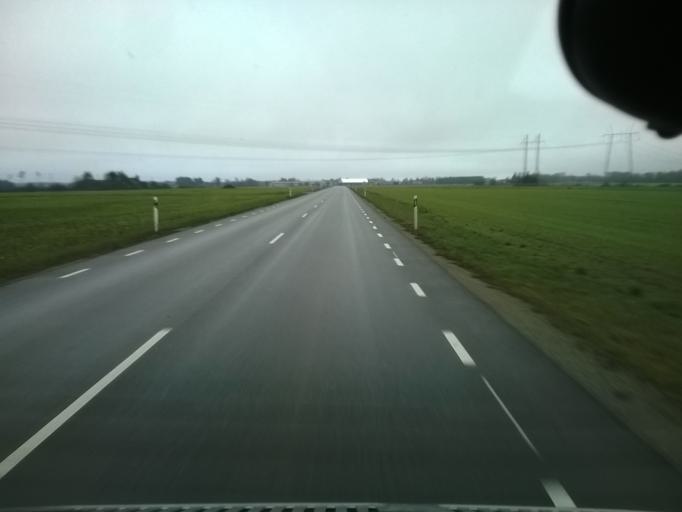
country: EE
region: Harju
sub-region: Saku vald
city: Saku
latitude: 59.2609
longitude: 24.7154
